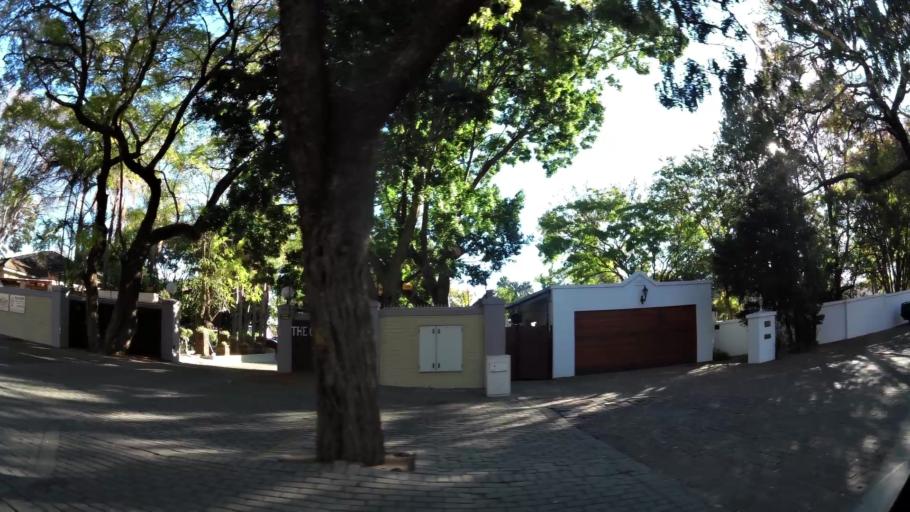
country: ZA
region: Limpopo
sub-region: Capricorn District Municipality
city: Polokwane
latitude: -23.9064
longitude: 29.4628
